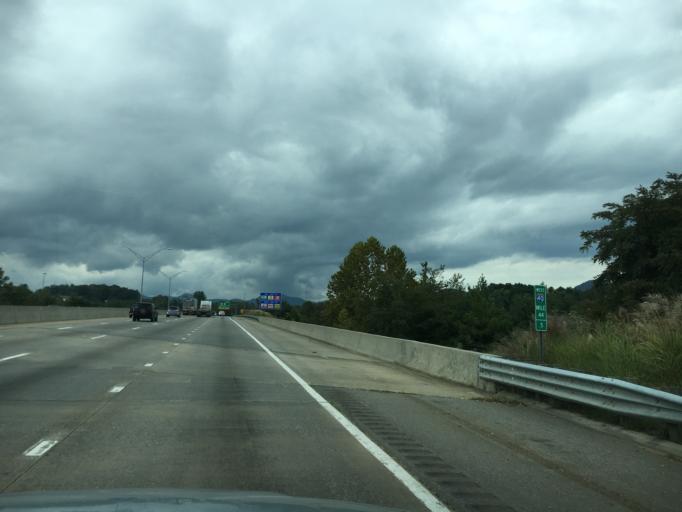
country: US
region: North Carolina
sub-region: Buncombe County
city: Bent Creek
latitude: 35.5590
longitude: -82.6347
